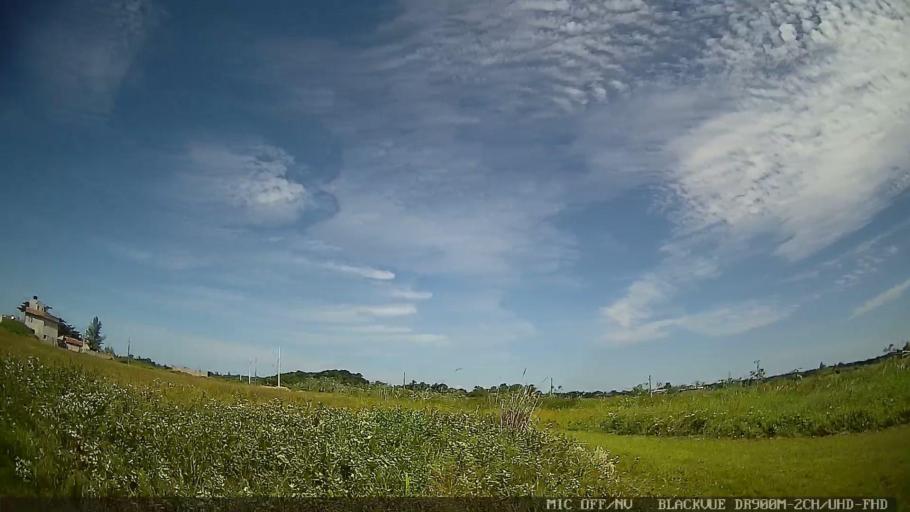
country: BR
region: Sao Paulo
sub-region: Iguape
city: Iguape
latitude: -24.7931
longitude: -47.6220
